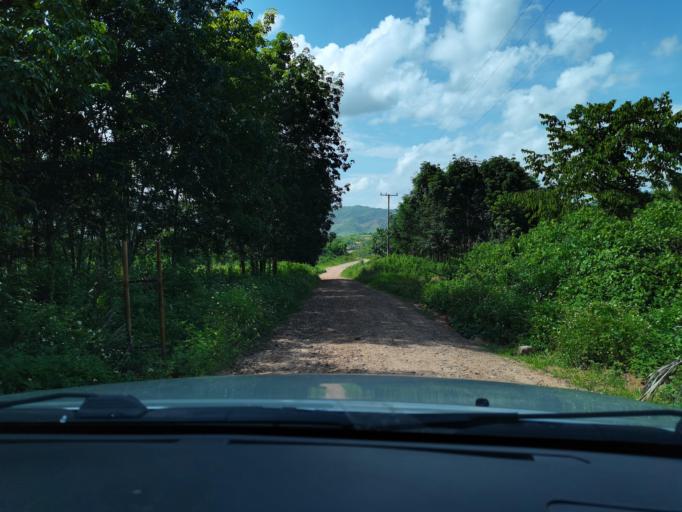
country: LA
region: Loungnamtha
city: Muang Nale
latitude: 20.5808
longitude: 101.0595
